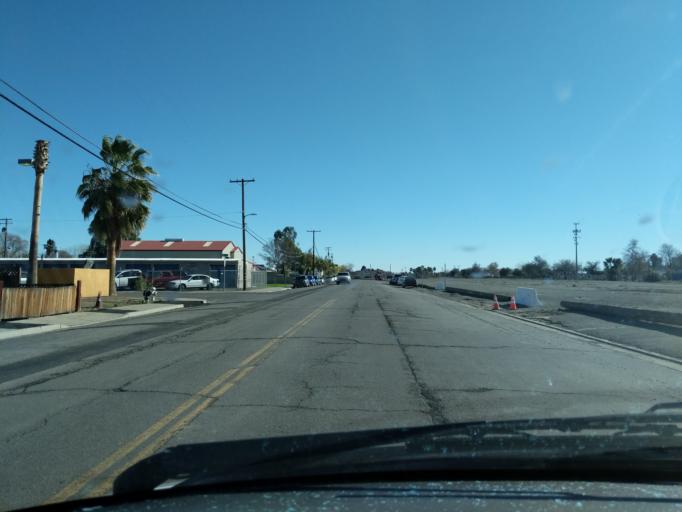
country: US
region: California
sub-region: Merced County
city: Los Banos
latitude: 37.0612
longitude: -120.8426
